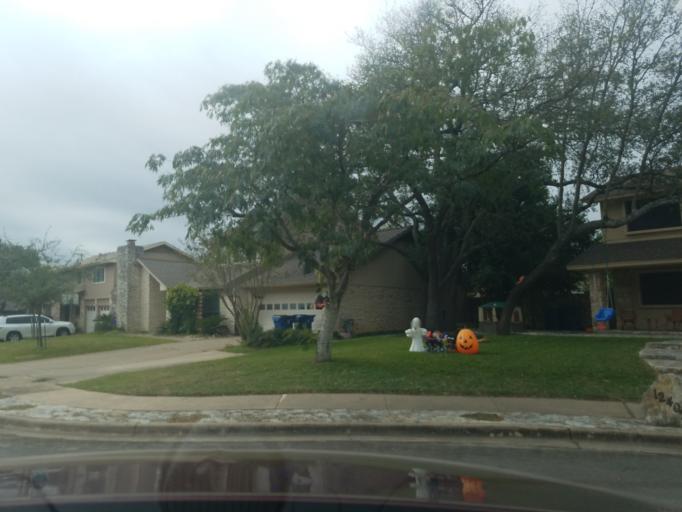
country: US
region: Texas
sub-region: Williamson County
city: Anderson Mill
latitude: 30.4636
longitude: -97.8094
